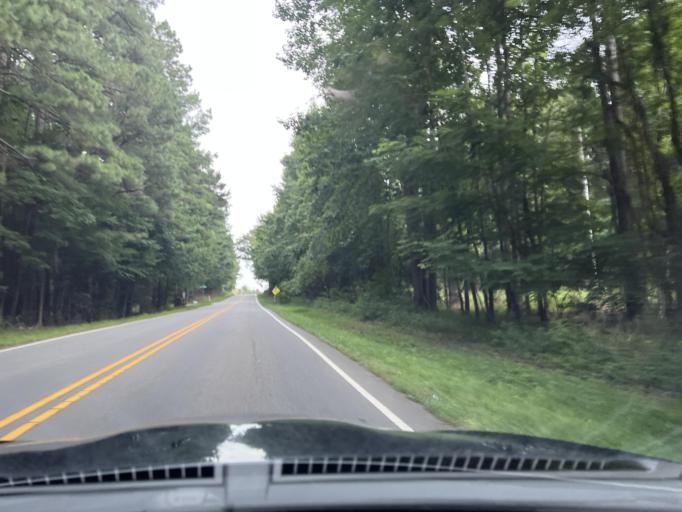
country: US
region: North Carolina
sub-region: Wake County
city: Wake Forest
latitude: 36.0061
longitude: -78.5250
